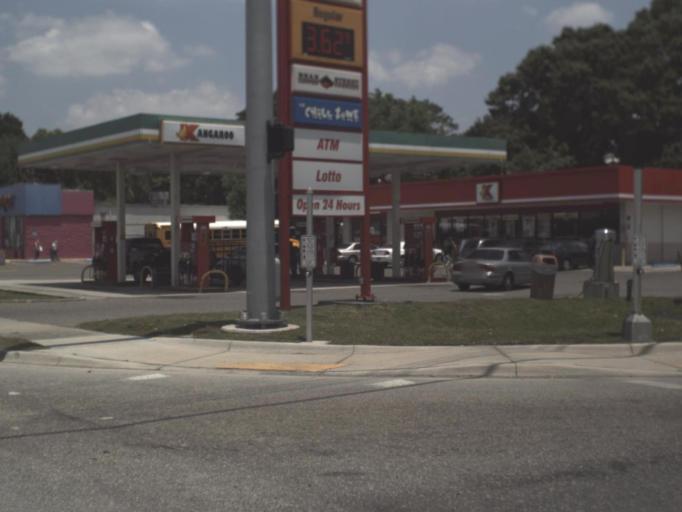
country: US
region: Florida
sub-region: Duval County
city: Jacksonville
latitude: 30.3365
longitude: -81.7310
